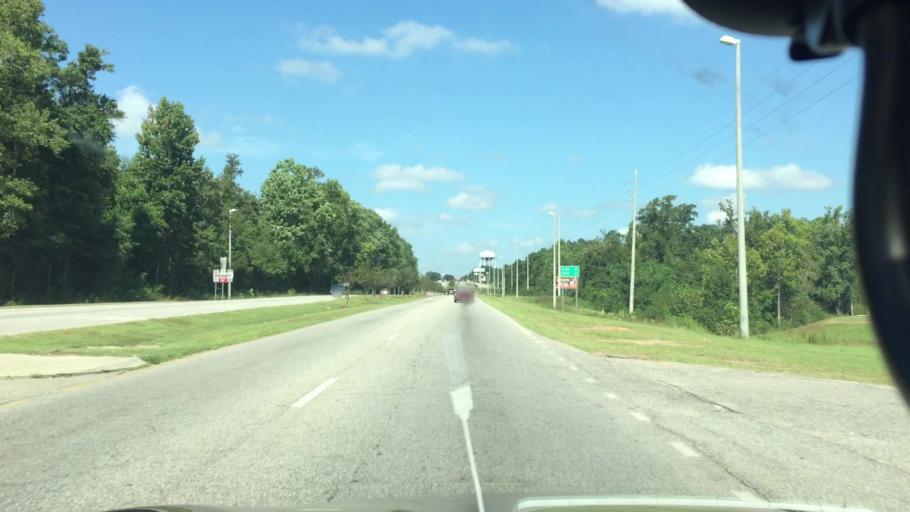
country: US
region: Alabama
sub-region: Coffee County
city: Enterprise
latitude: 31.3297
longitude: -85.8398
